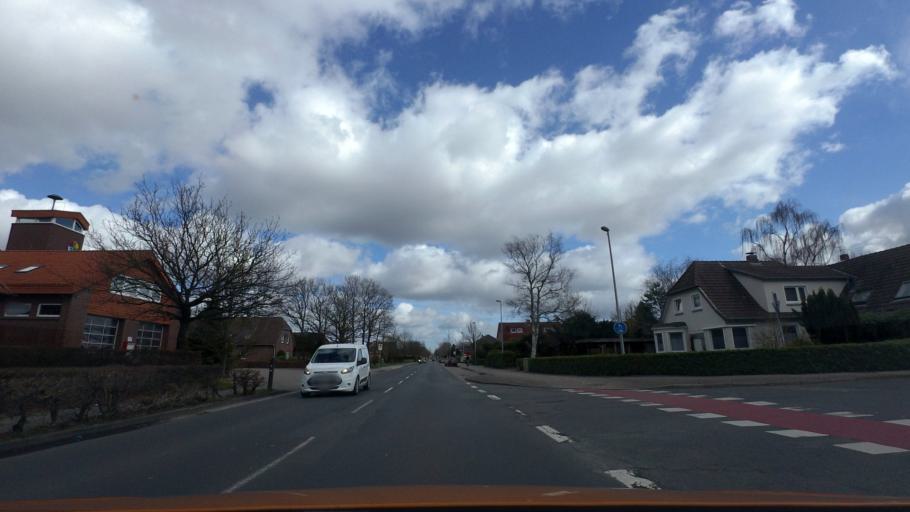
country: DE
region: Lower Saxony
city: Oldenburg
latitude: 53.1393
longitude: 8.1168
